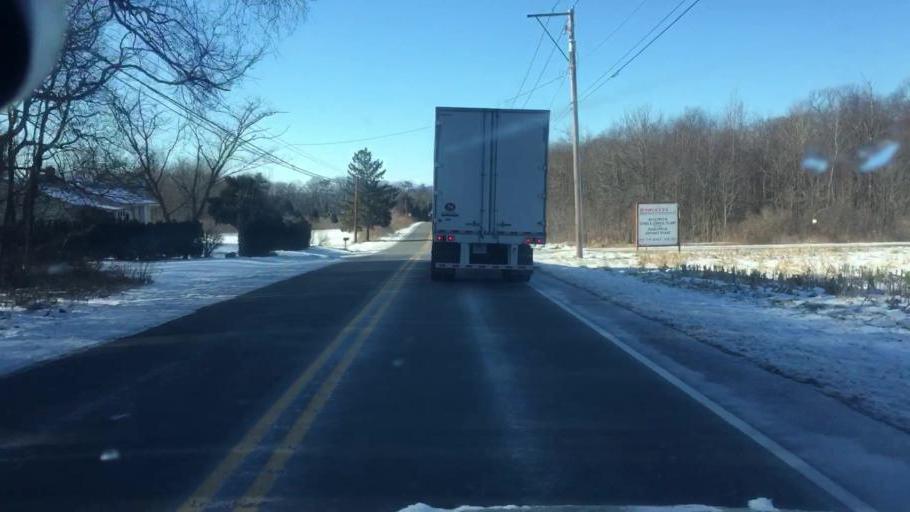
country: US
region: Pennsylvania
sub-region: Luzerne County
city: Nescopeck
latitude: 41.0548
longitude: -76.1773
